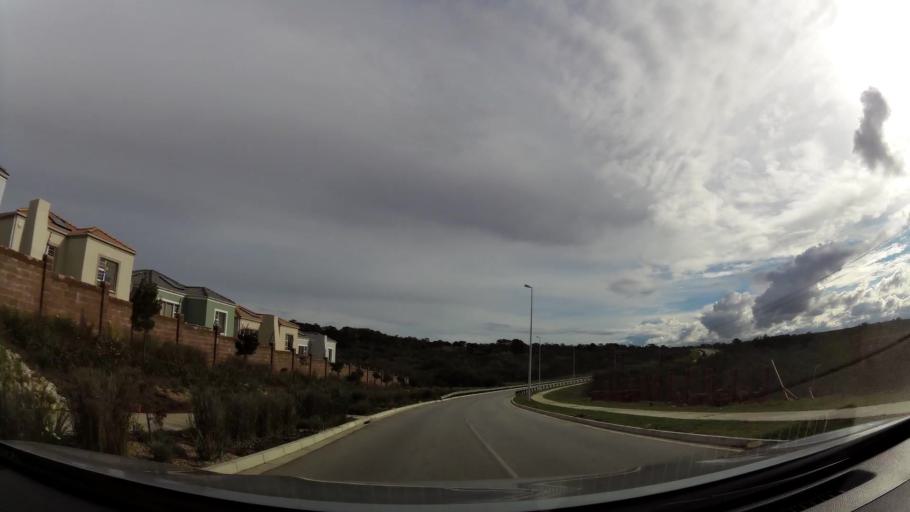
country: ZA
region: Eastern Cape
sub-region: Nelson Mandela Bay Metropolitan Municipality
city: Port Elizabeth
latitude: -33.9308
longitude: 25.4989
